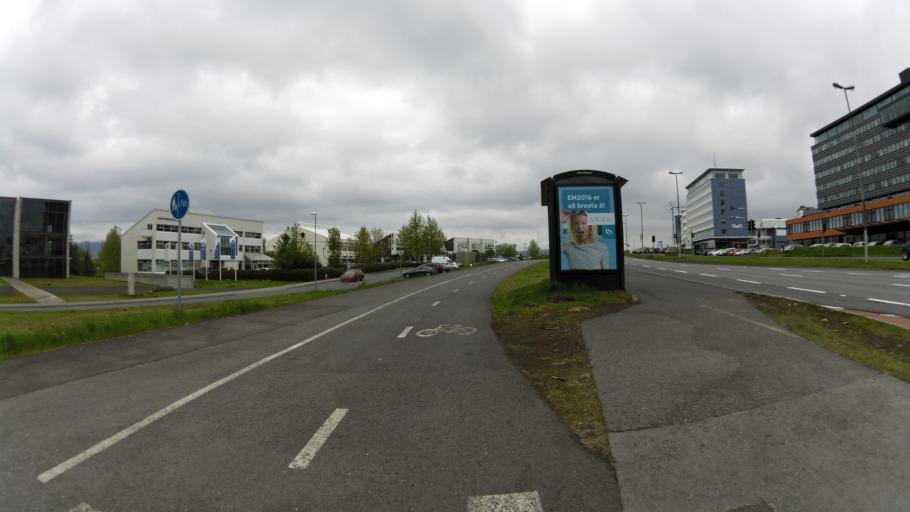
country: IS
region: Capital Region
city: Reykjavik
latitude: 64.1403
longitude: -21.8904
